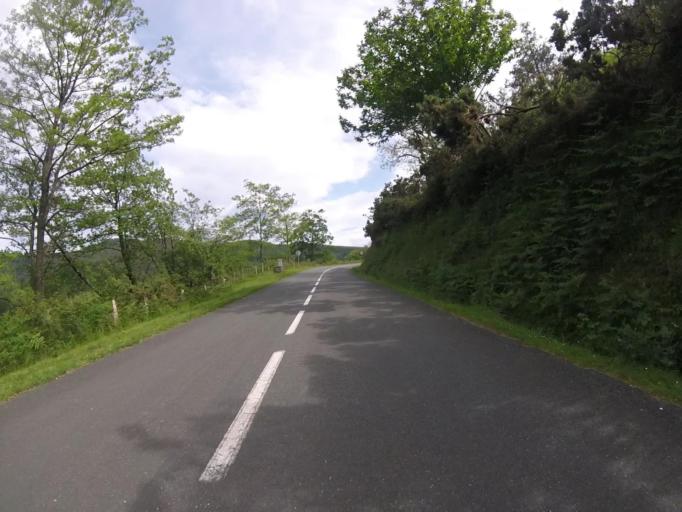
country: ES
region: Navarre
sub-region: Provincia de Navarra
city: Arano
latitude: 43.2509
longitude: -1.8458
